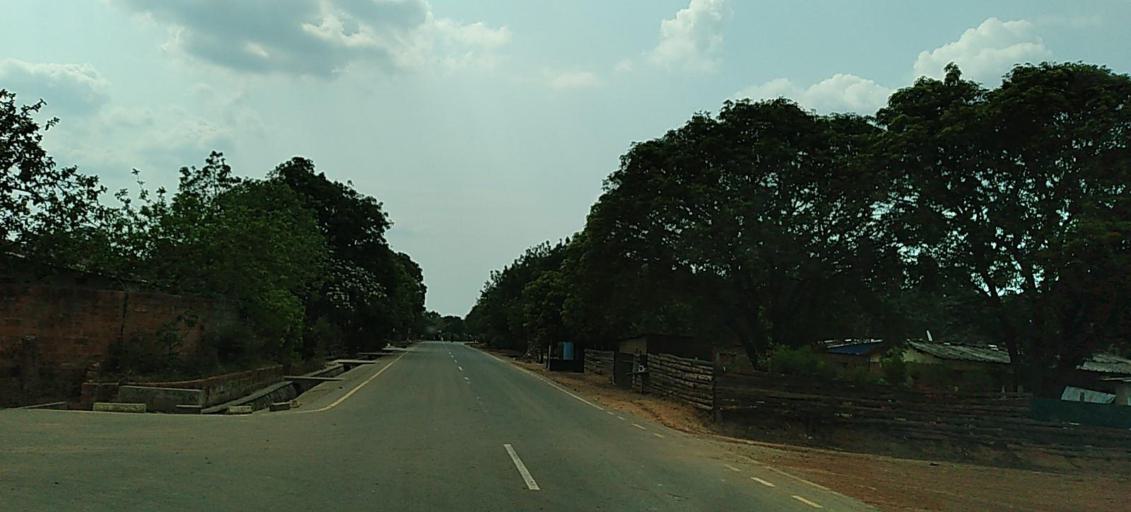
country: ZM
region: Copperbelt
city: Kalulushi
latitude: -12.8559
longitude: 28.1318
